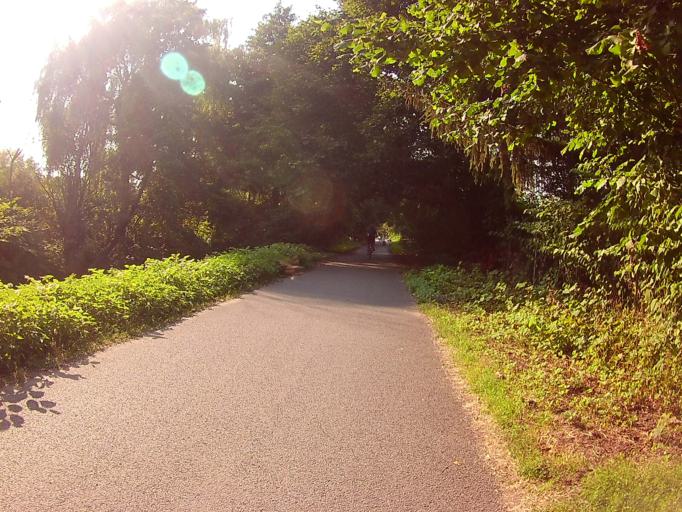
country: DE
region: Berlin
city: Kopenick Bezirk
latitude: 52.4669
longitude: 13.5707
